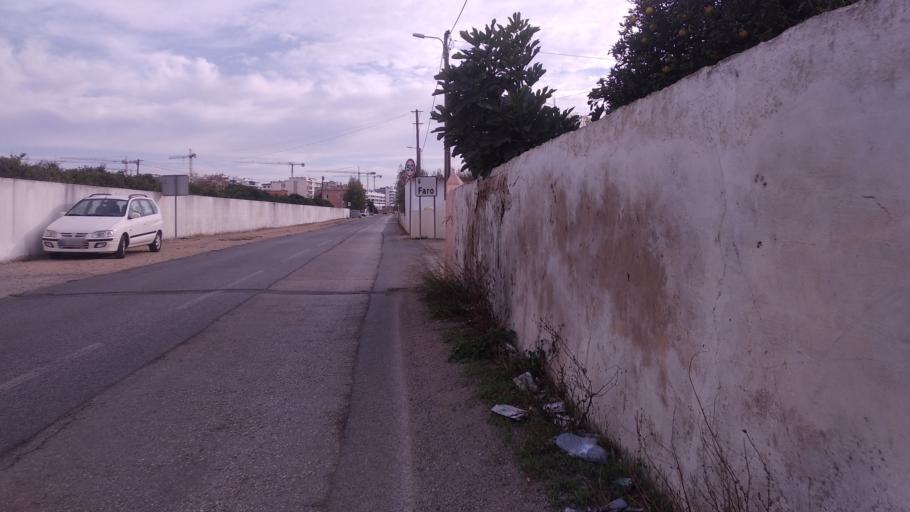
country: PT
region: Faro
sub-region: Faro
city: Faro
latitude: 37.0373
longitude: -7.9404
